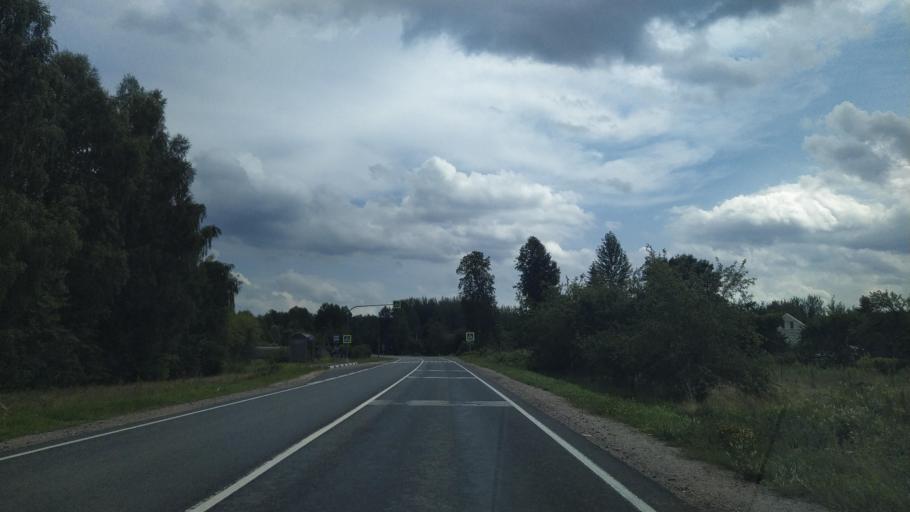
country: RU
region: Pskov
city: Pskov
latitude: 57.8360
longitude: 28.5112
